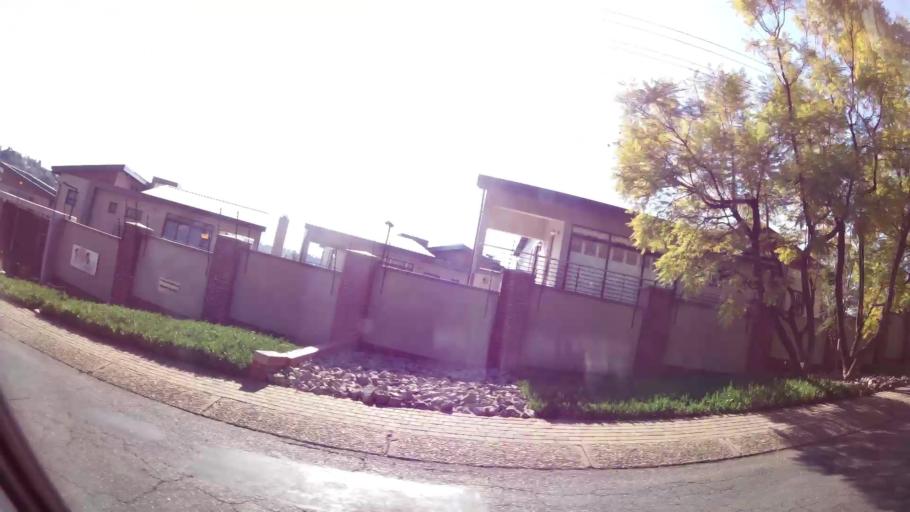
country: ZA
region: Gauteng
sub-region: City of Tshwane Metropolitan Municipality
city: Pretoria
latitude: -25.7909
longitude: 28.2540
